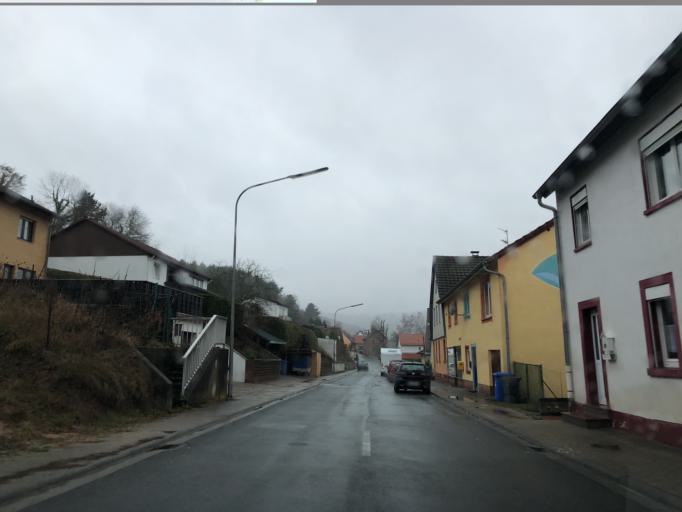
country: DE
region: Hesse
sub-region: Regierungsbezirk Darmstadt
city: Lutzelbach
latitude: 49.7665
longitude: 9.1037
